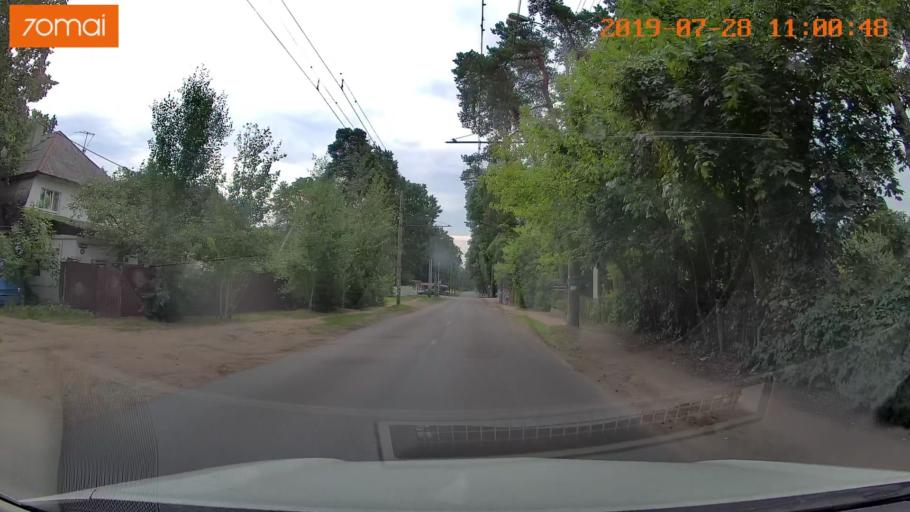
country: RU
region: Kaliningrad
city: Vzmorye
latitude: 54.7252
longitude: 20.3638
